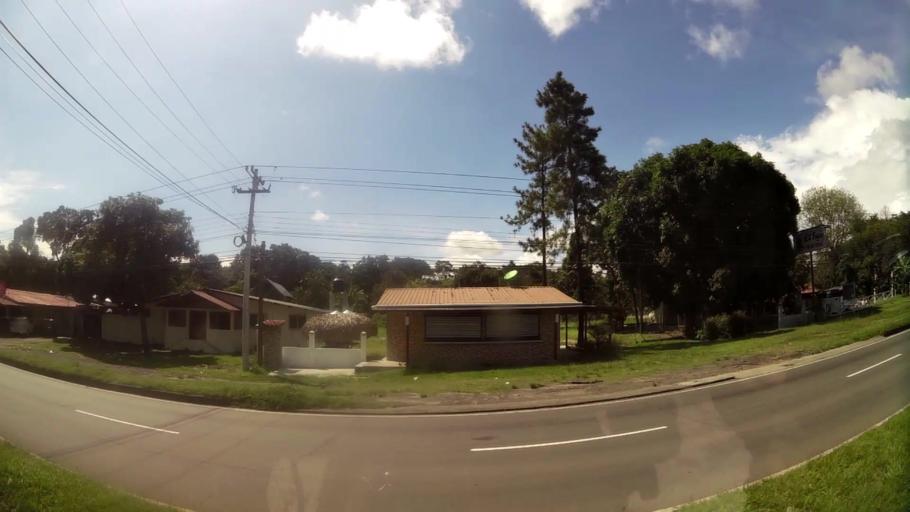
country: PA
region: Panama
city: Chame
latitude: 8.5836
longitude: -79.8843
